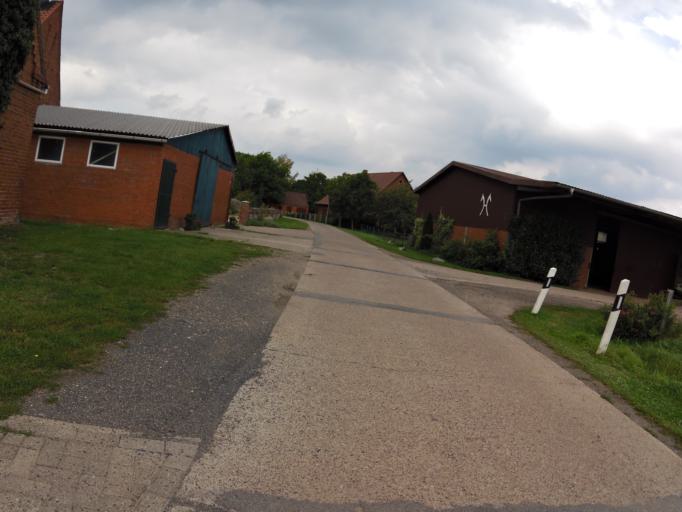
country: DE
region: Lower Saxony
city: Blender
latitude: 52.9129
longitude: 9.1598
